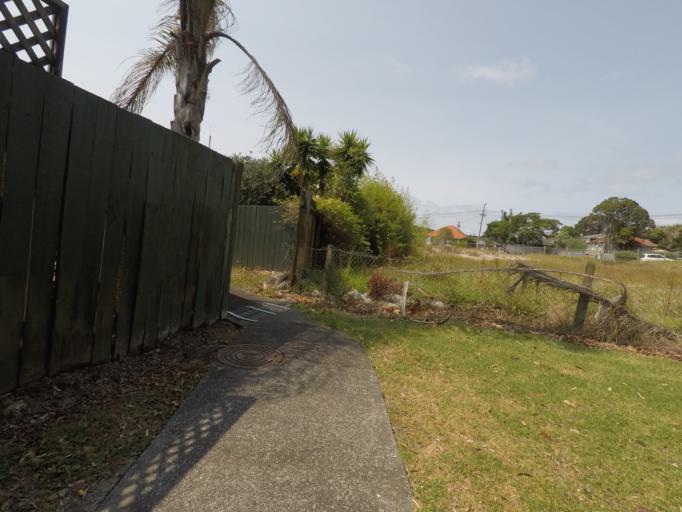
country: NZ
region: Auckland
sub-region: Auckland
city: Waitakere
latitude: -36.9150
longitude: 174.6901
